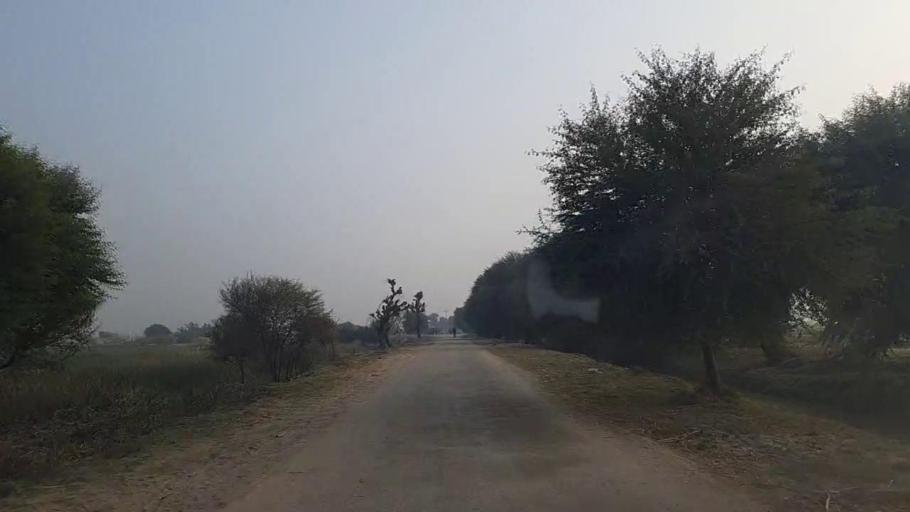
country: PK
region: Sindh
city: Sinjhoro
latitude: 26.1171
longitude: 68.8040
